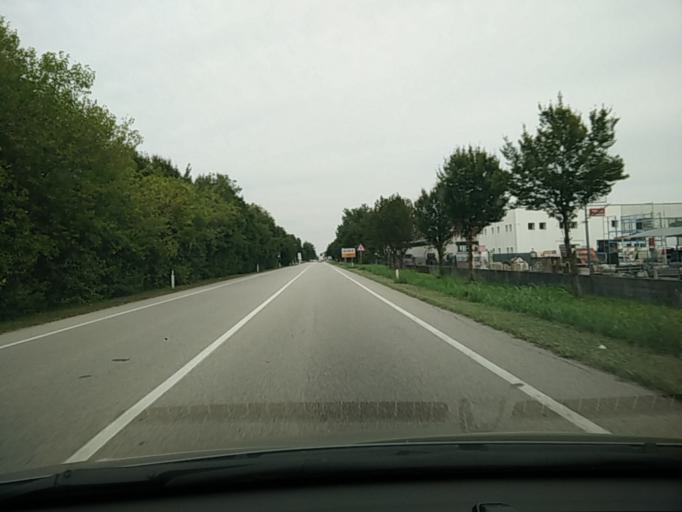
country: IT
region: Veneto
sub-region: Provincia di Treviso
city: Roncade
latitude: 45.6392
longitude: 12.3876
